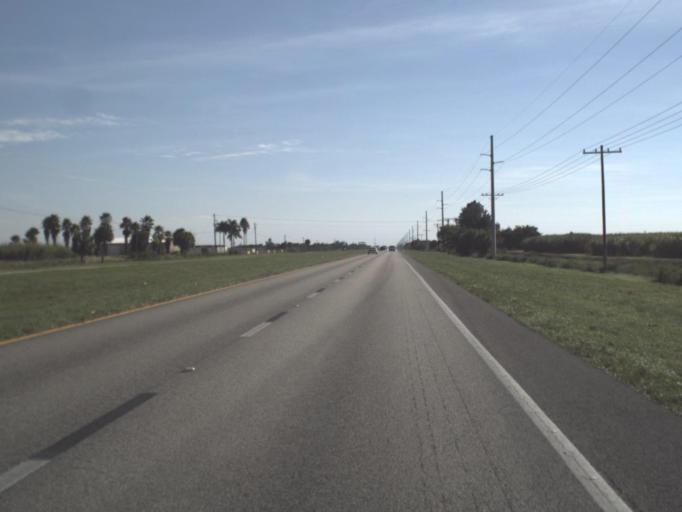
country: US
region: Florida
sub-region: Glades County
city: Moore Haven
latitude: 26.8202
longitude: -81.0826
